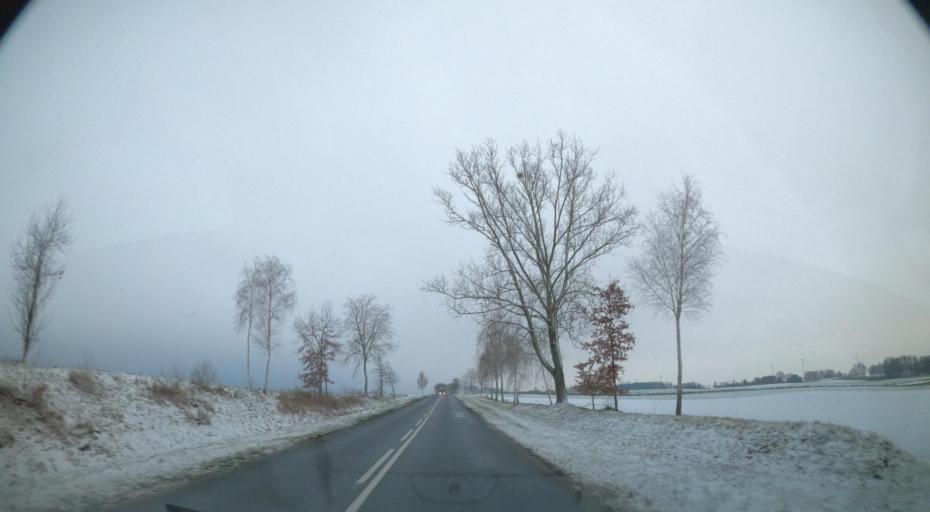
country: PL
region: Kujawsko-Pomorskie
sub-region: Powiat lipnowski
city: Dobrzyn nad Wisla
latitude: 52.6544
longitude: 19.3878
